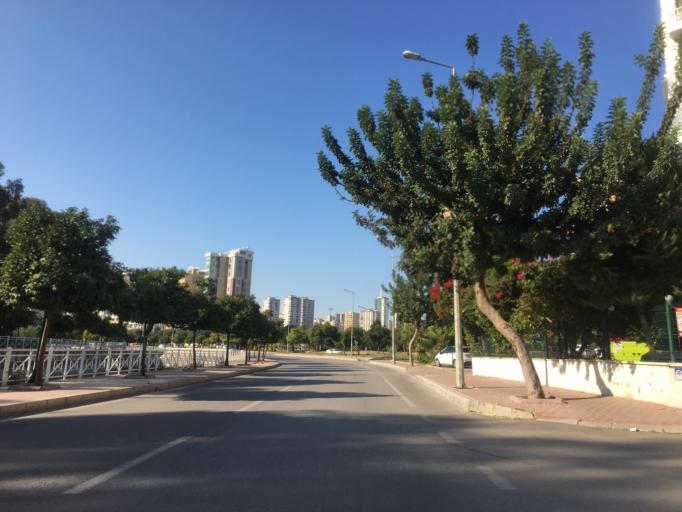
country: TR
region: Adana
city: Seyhan
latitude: 37.0280
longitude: 35.2719
